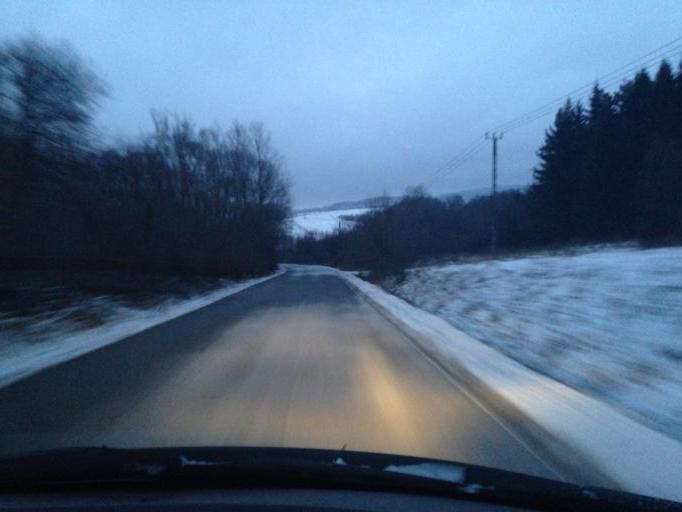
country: PL
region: Subcarpathian Voivodeship
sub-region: Powiat jasielski
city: Krempna
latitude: 49.5216
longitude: 21.5471
